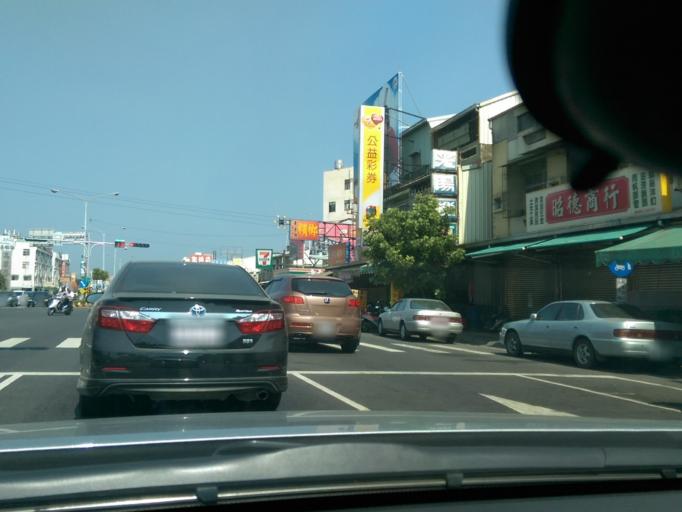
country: TW
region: Taiwan
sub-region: Chiayi
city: Jiayi Shi
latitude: 23.5235
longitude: 120.4396
